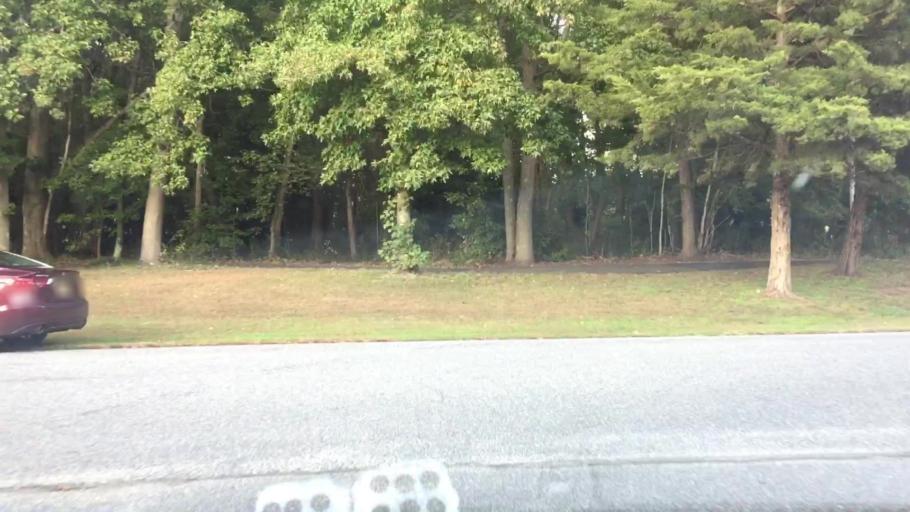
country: US
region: New Jersey
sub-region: Gloucester County
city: Pitman
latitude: 39.7417
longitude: -75.0950
